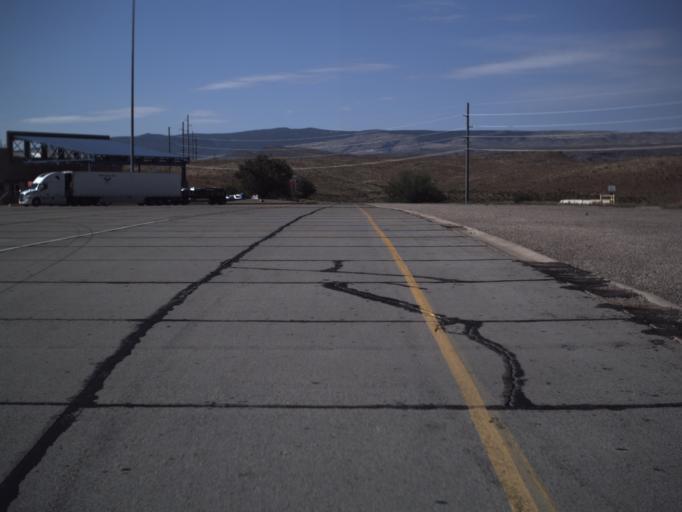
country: US
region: Utah
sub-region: Washington County
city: Saint George
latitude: 37.0139
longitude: -113.6156
